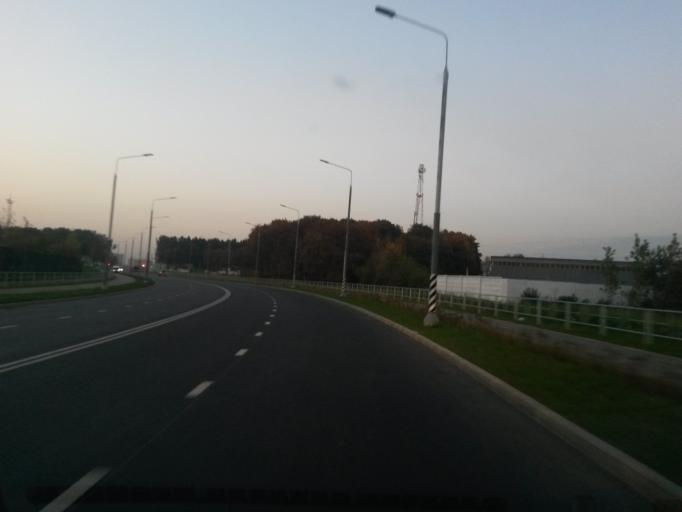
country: RU
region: Moskovskaya
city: Kommunarka
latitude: 55.5560
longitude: 37.4913
